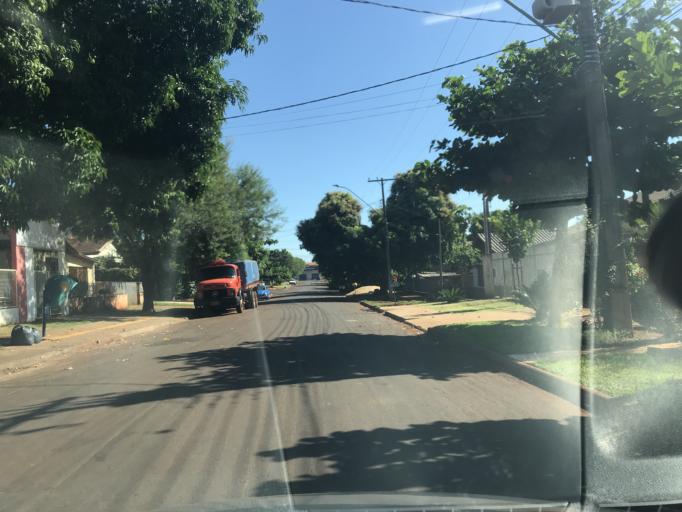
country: BR
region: Parana
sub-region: Palotina
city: Palotina
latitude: -24.2811
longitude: -53.8248
